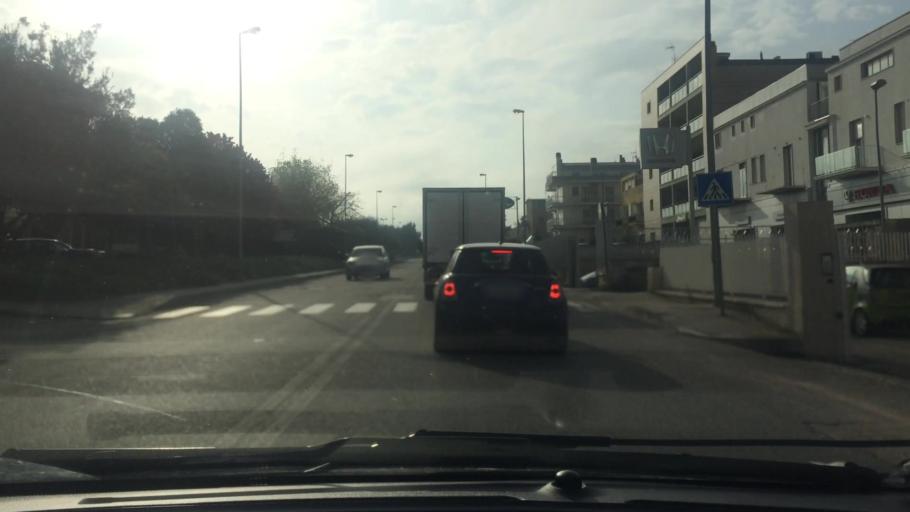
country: IT
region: Basilicate
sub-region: Provincia di Matera
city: Matera
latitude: 40.6812
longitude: 16.5820
